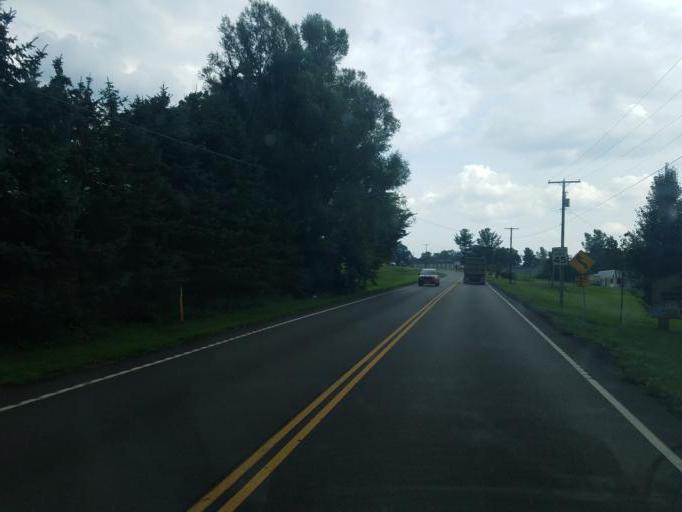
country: US
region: Ohio
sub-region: Knox County
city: Mount Vernon
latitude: 40.4126
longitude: -82.4987
